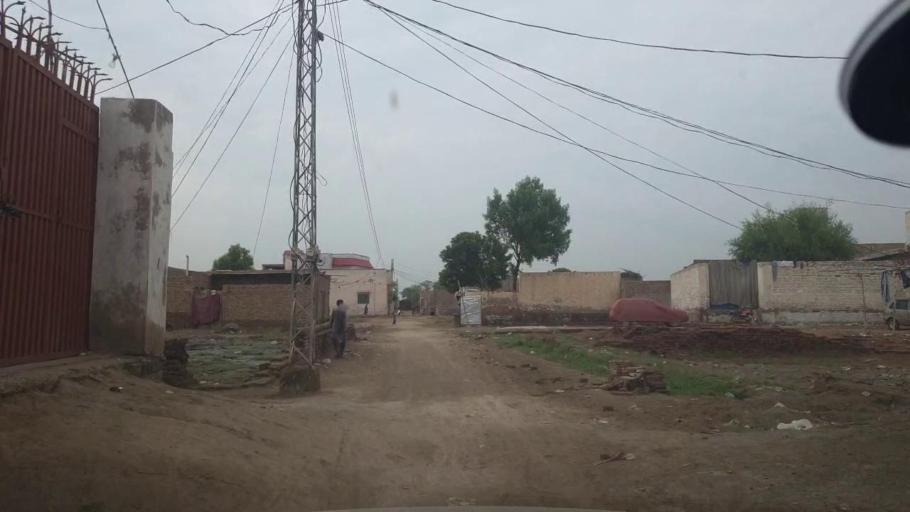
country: PK
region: Sindh
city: Jacobabad
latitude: 28.2573
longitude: 68.4511
